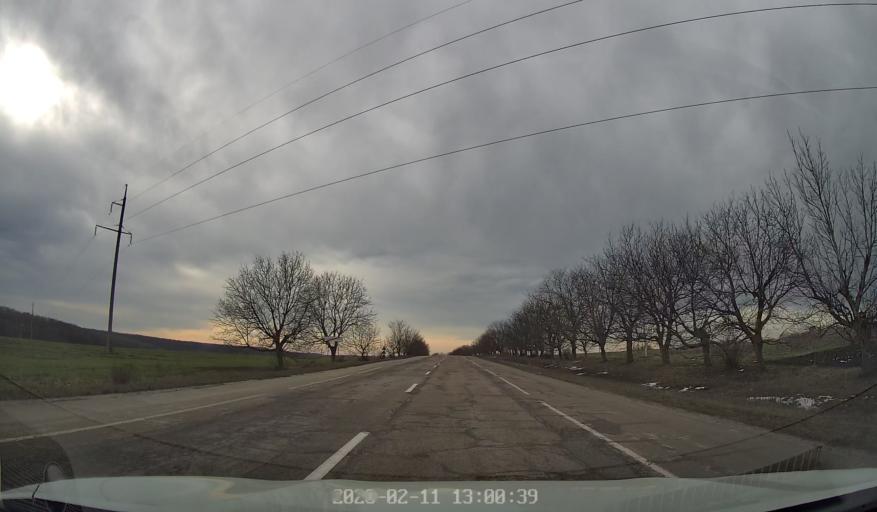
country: MD
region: Briceni
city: Briceni
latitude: 48.3242
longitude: 27.0159
